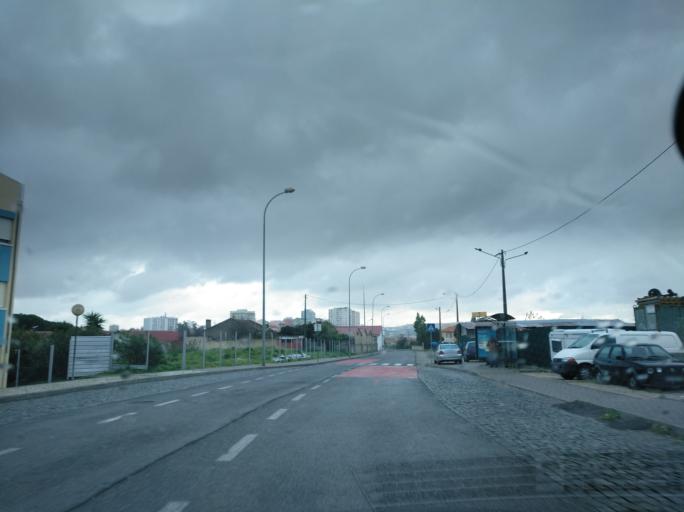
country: PT
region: Lisbon
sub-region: Odivelas
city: Pontinha
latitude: 38.7691
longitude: -9.1955
